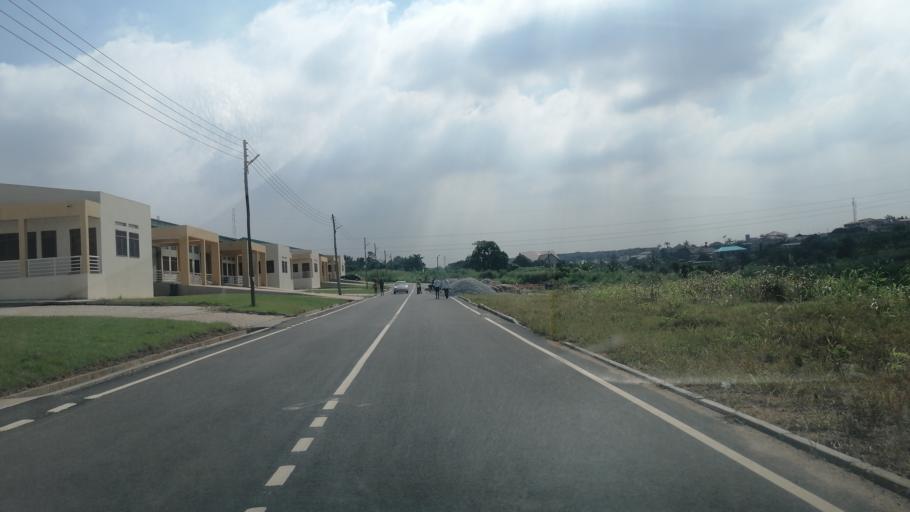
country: GH
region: Ashanti
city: Kumasi
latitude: 6.6999
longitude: -1.6797
